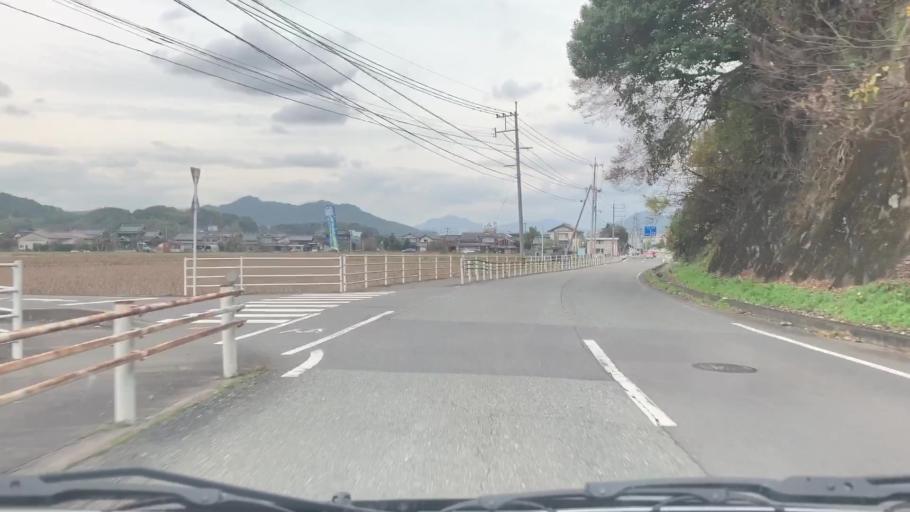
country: JP
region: Saga Prefecture
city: Kashima
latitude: 33.1194
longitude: 130.0635
